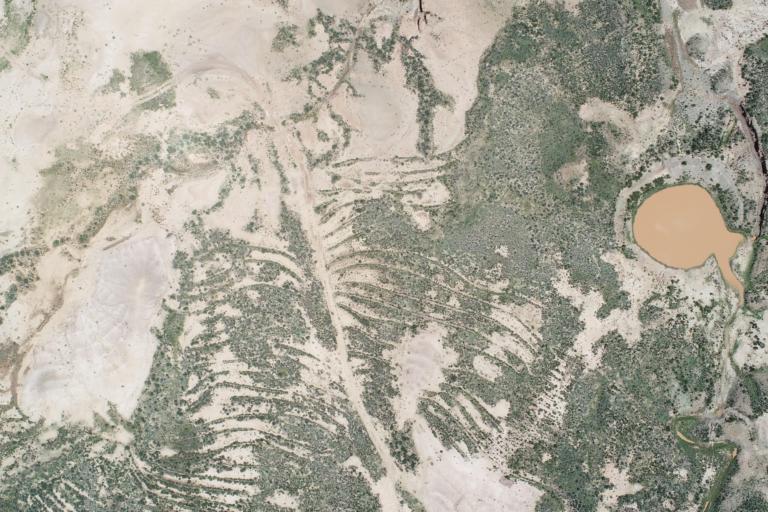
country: BO
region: La Paz
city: Curahuara de Carangas
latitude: -17.3167
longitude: -68.4951
